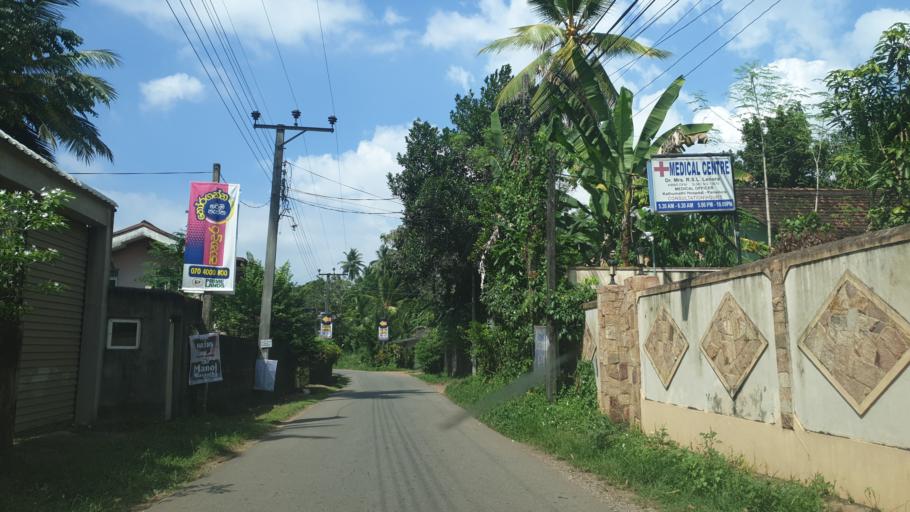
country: LK
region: Western
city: Horana South
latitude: 6.7084
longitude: 79.9833
